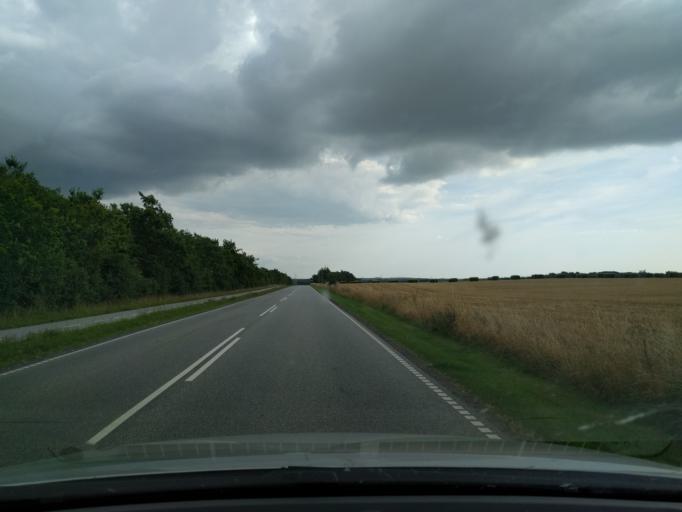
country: DK
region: Central Jutland
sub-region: Herning Kommune
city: Snejbjerg
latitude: 56.1144
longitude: 8.9077
